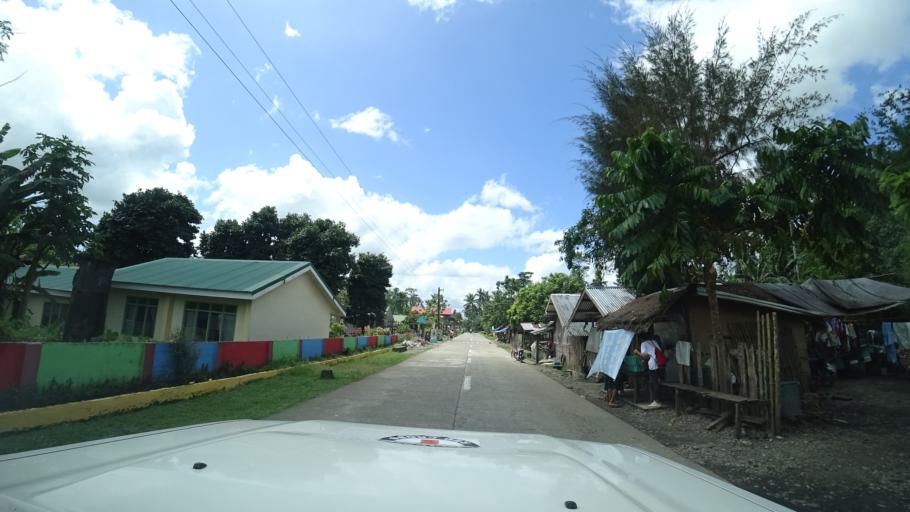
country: PH
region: Eastern Visayas
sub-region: Province of Leyte
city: La Paz
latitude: 10.8613
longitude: 124.9488
